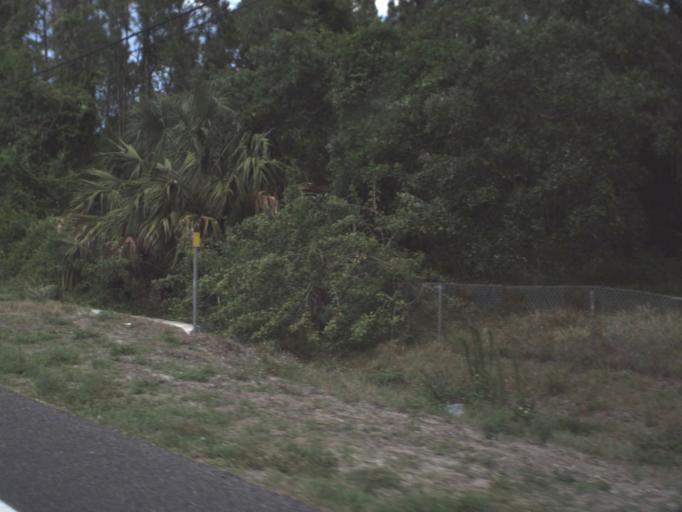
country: US
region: Florida
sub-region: Brevard County
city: Mims
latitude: 28.7179
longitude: -80.8632
